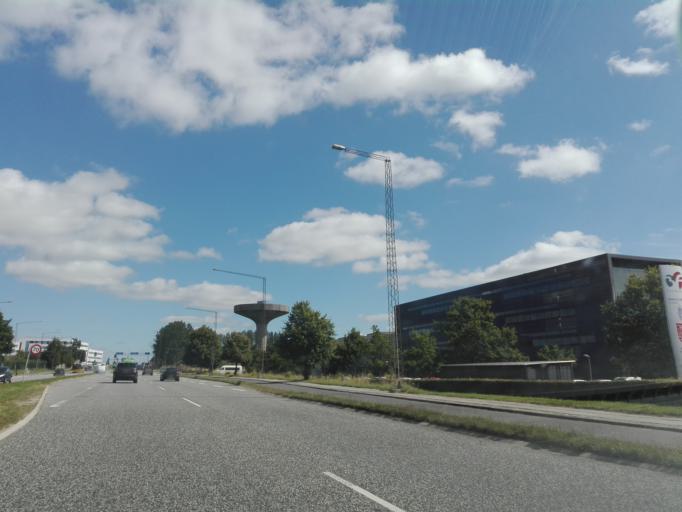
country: DK
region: Central Jutland
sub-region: Arhus Kommune
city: Stavtrup
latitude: 56.1682
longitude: 10.1521
